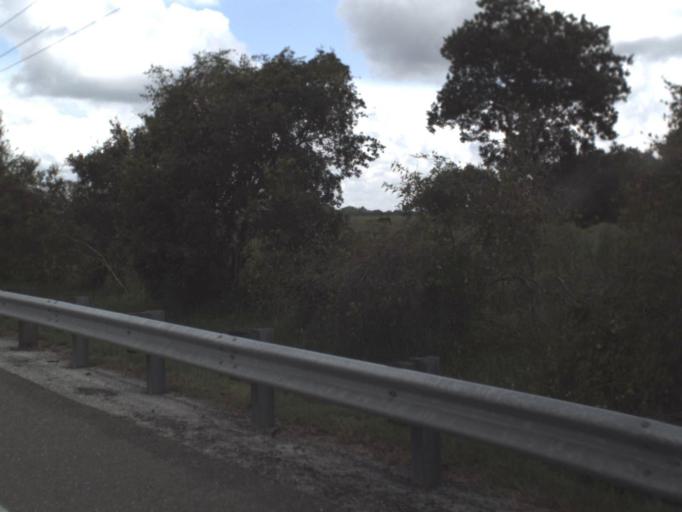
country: US
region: Florida
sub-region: Hardee County
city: Zolfo Springs
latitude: 27.4822
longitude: -81.9048
